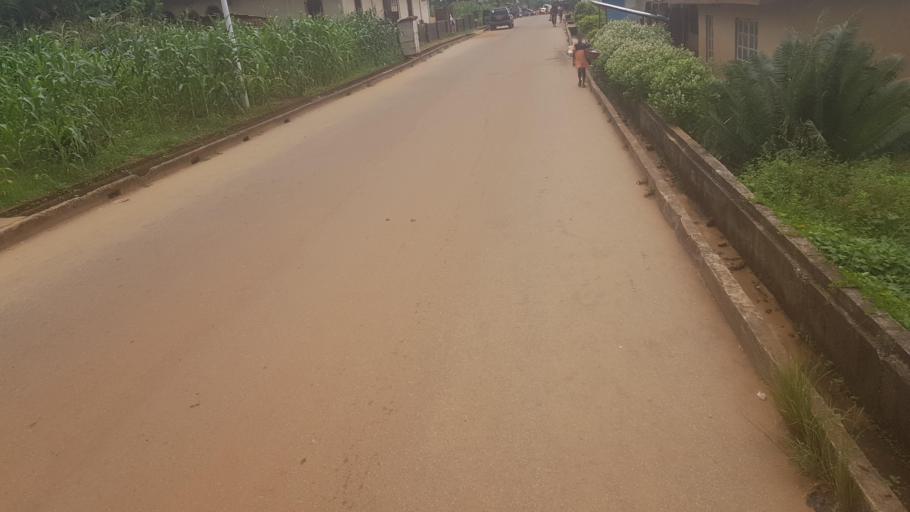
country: SL
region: Southern Province
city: Mogbwemo
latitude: 7.6065
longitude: -12.1805
